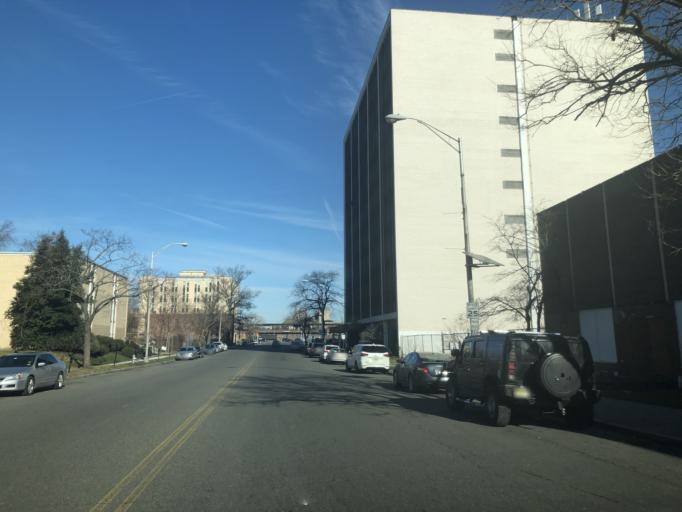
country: US
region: New Jersey
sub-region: Essex County
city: Orange
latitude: 40.7628
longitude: -74.2215
